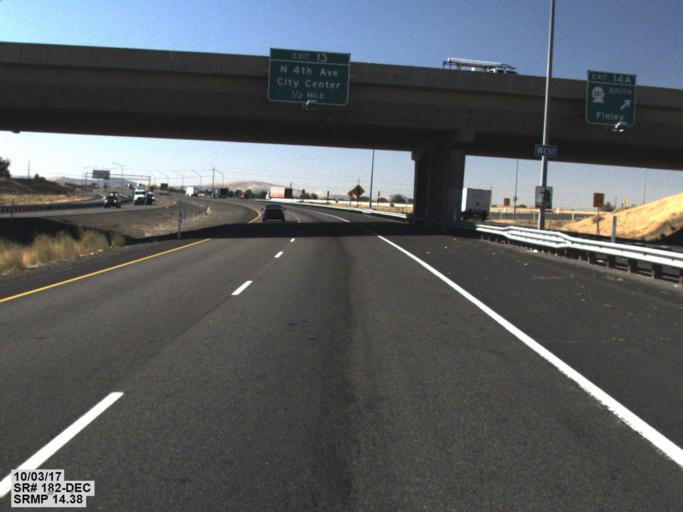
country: US
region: Washington
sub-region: Franklin County
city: Pasco
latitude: 46.2519
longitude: -119.0825
